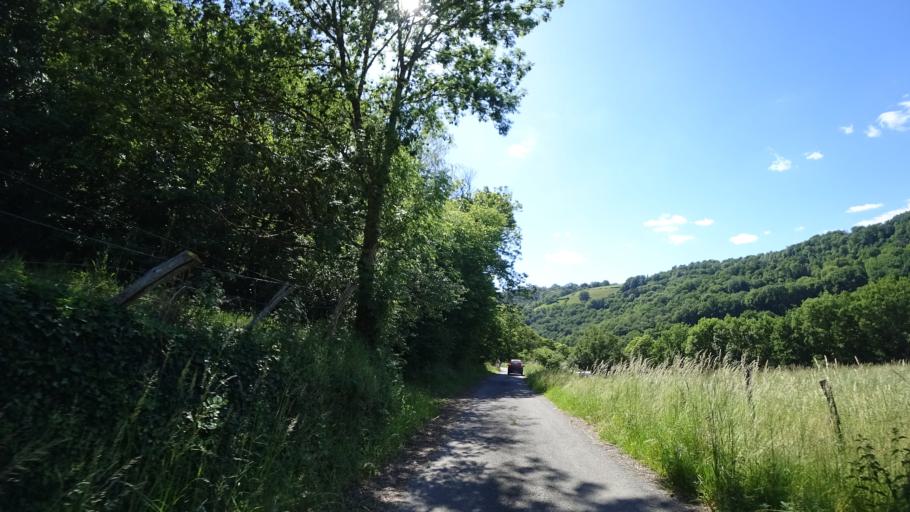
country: FR
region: Midi-Pyrenees
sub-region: Departement de l'Aveyron
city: Colombies
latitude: 44.3838
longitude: 2.3300
